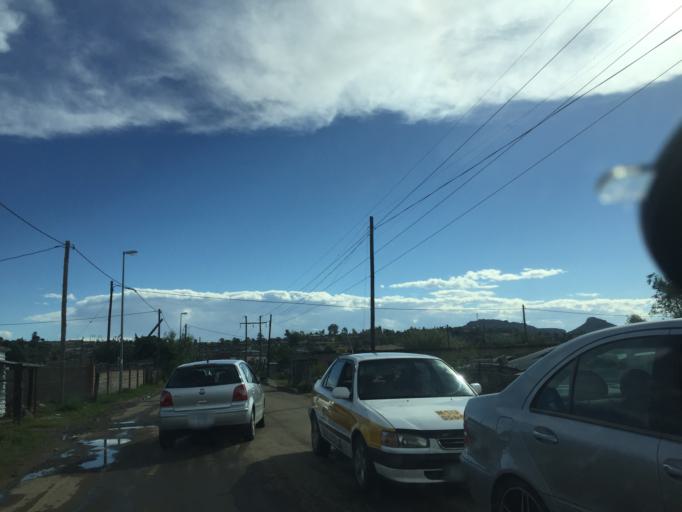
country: LS
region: Maseru
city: Maseru
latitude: -29.3190
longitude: 27.5365
